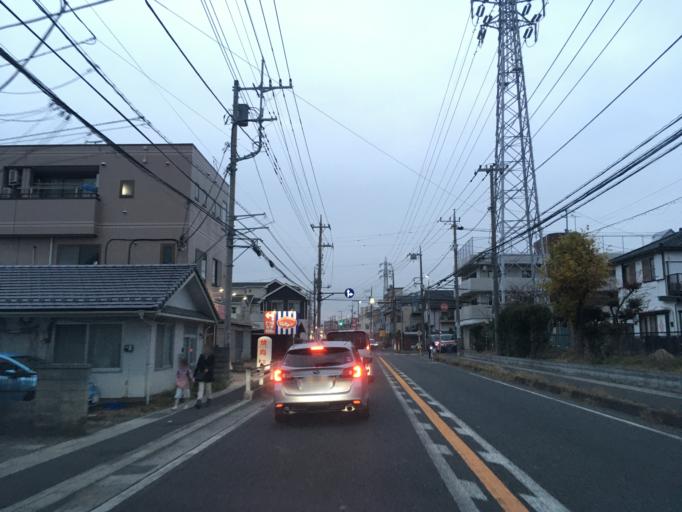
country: JP
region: Kanagawa
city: Minami-rinkan
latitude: 35.4727
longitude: 139.4656
